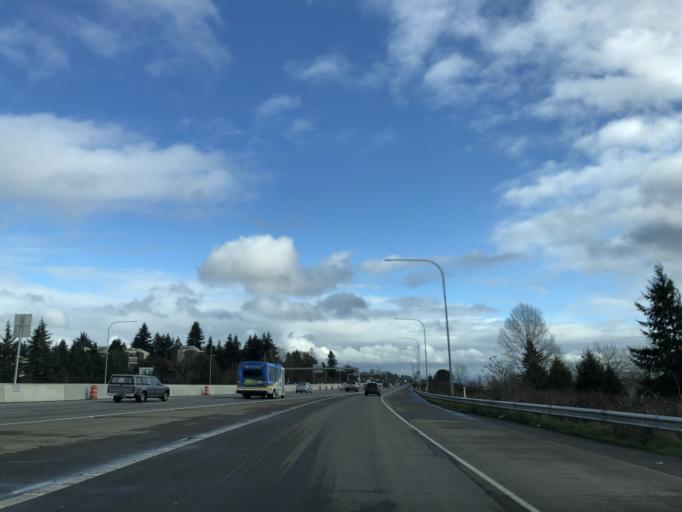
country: US
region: Washington
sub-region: Pierce County
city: Fircrest
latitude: 47.2347
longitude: -122.4793
